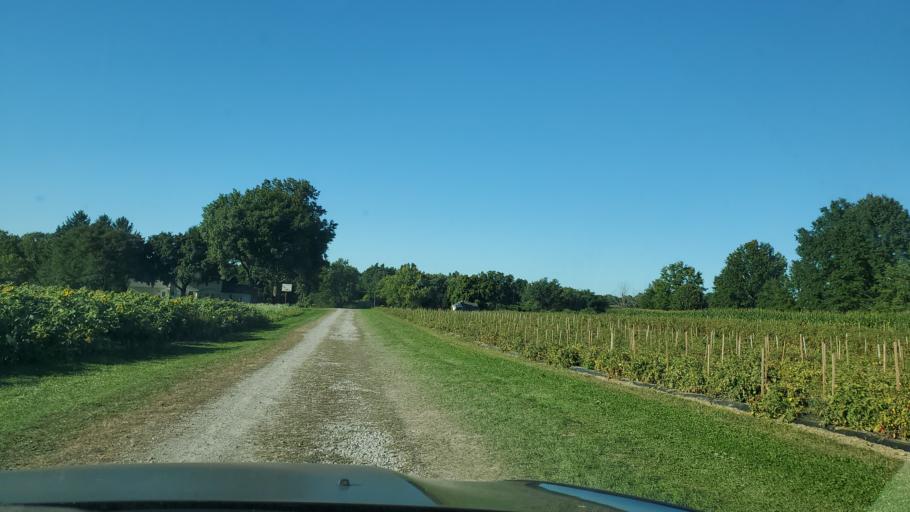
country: US
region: Ohio
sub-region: Mahoning County
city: Canfield
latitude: 40.9853
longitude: -80.8027
